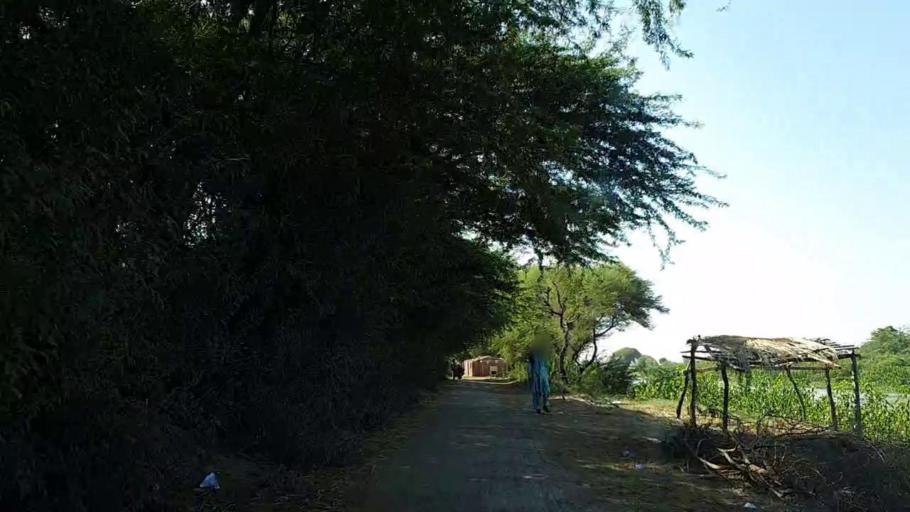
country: PK
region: Sindh
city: Chuhar Jamali
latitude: 24.5718
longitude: 68.0437
